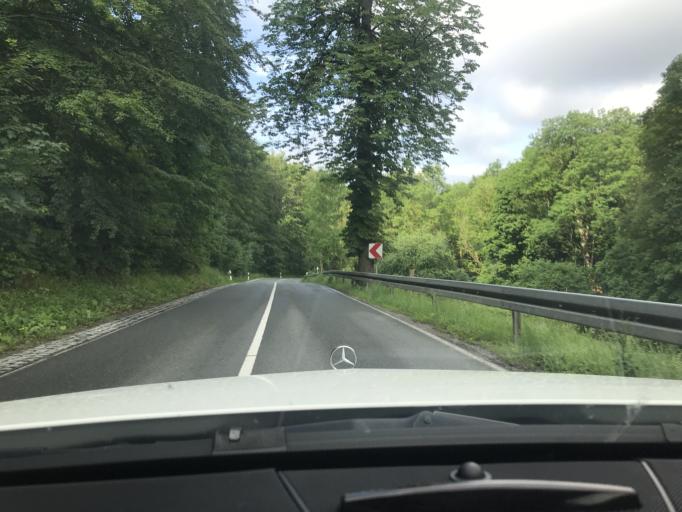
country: DE
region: Thuringia
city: Effelder
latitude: 51.2154
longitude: 10.2757
